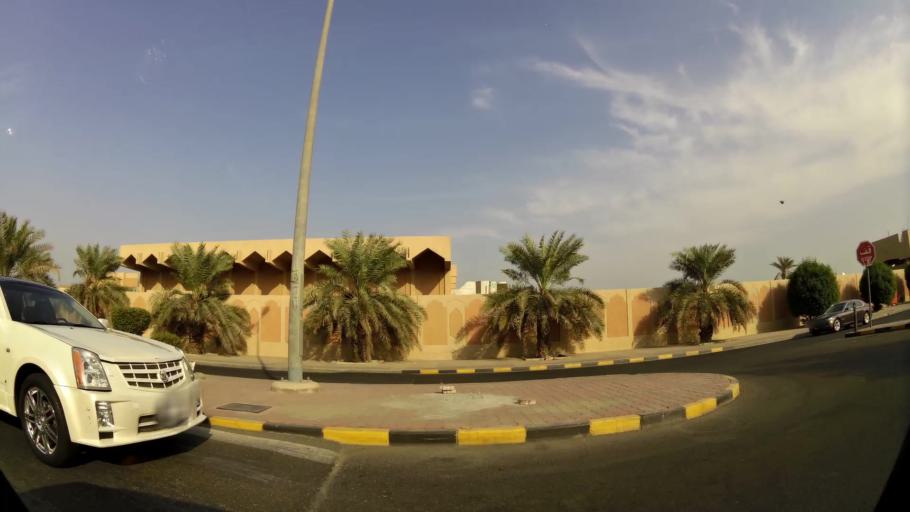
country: KW
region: Muhafazat Hawalli
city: Hawalli
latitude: 29.3294
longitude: 48.0018
